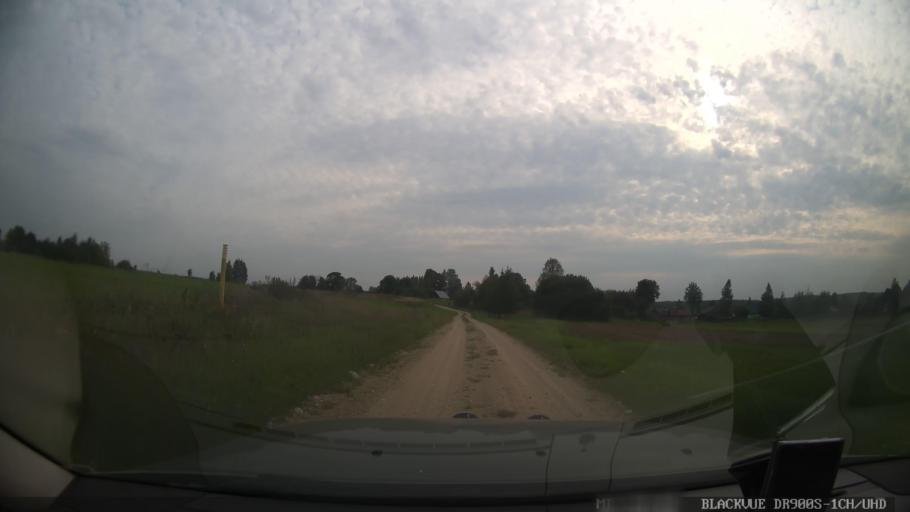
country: BY
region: Grodnenskaya
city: Ashmyany
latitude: 54.5327
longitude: 25.6707
